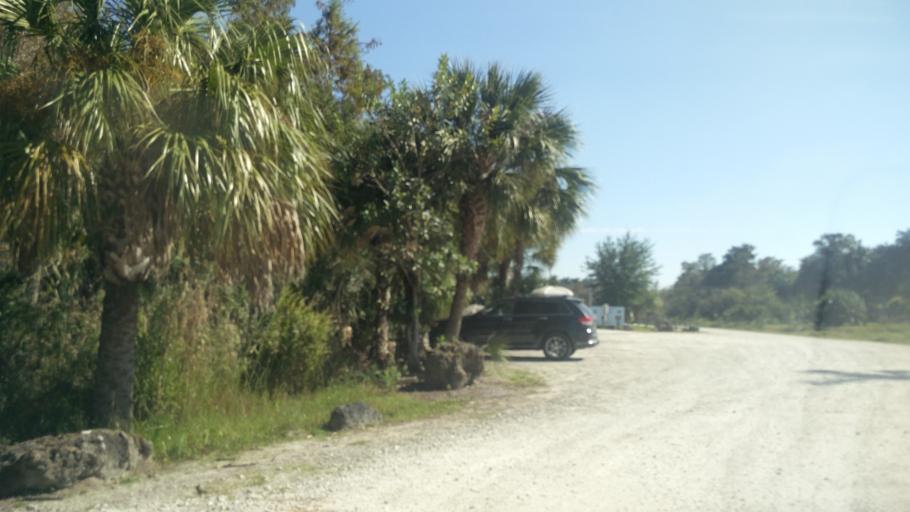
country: US
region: Florida
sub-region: Collier County
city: Lely Resort
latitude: 25.9516
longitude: -81.3606
